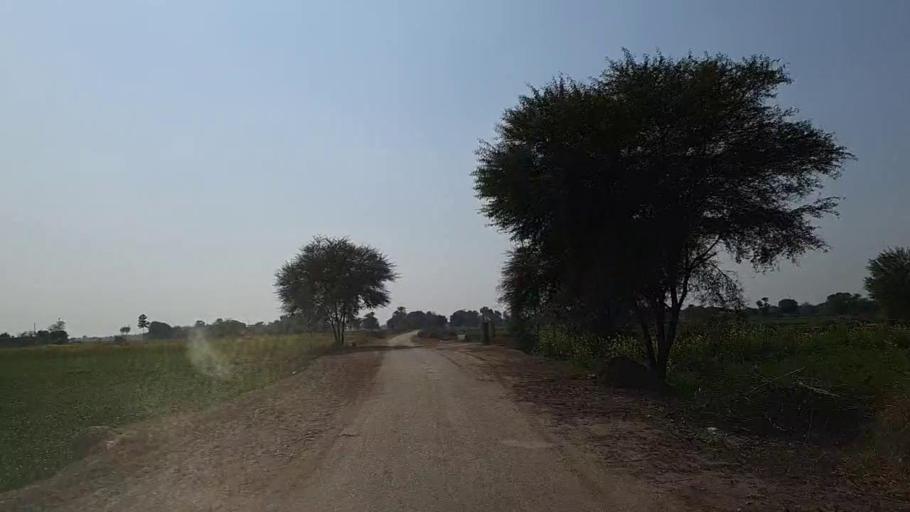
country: PK
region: Sindh
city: Nawabshah
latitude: 26.2508
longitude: 68.4862
